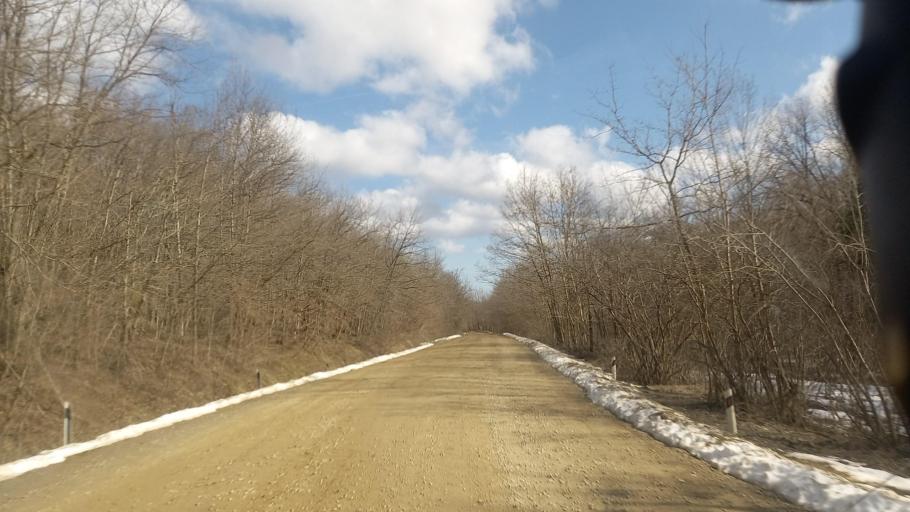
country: RU
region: Krasnodarskiy
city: Smolenskaya
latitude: 44.6057
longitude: 38.7765
